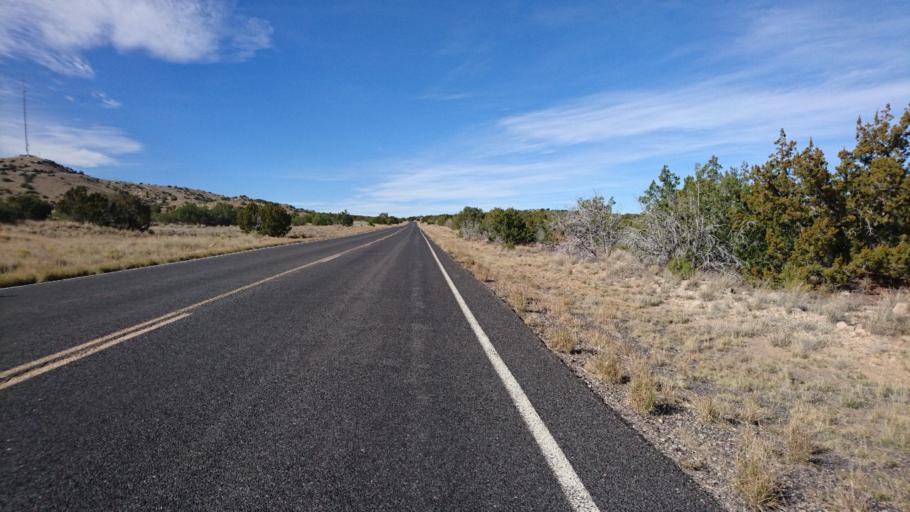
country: US
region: New Mexico
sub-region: Cibola County
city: Laguna
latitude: 35.0422
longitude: -107.3539
